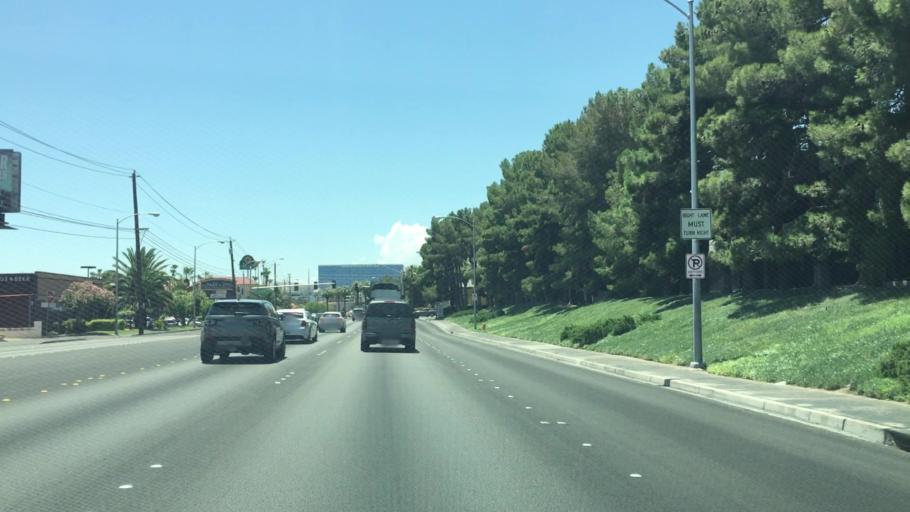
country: US
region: Nevada
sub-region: Clark County
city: Paradise
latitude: 36.1199
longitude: -115.1551
